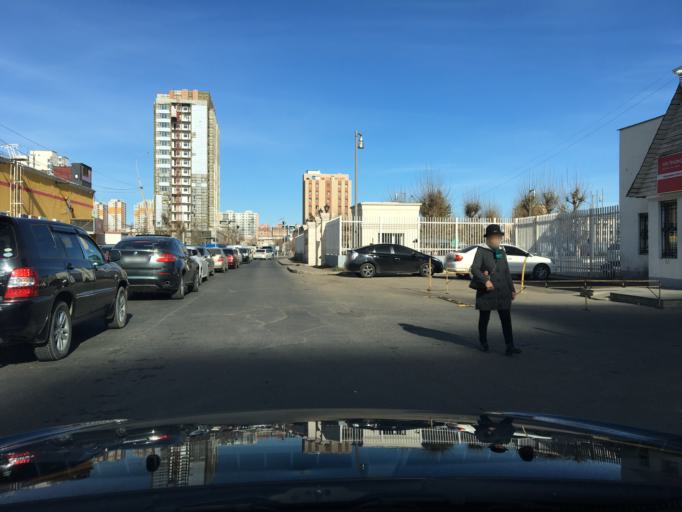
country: MN
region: Ulaanbaatar
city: Ulaanbaatar
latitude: 47.8978
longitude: 106.9018
